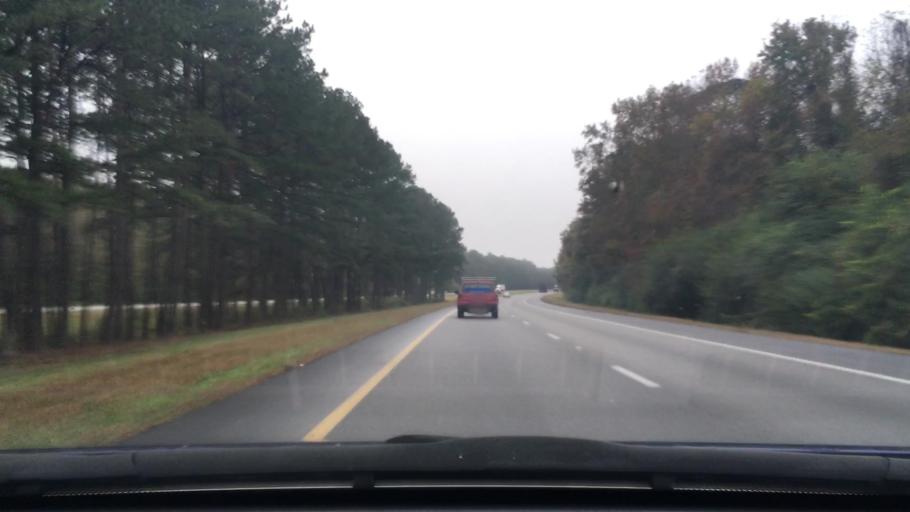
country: US
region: South Carolina
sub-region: Lee County
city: Bishopville
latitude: 34.1955
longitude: -80.3301
